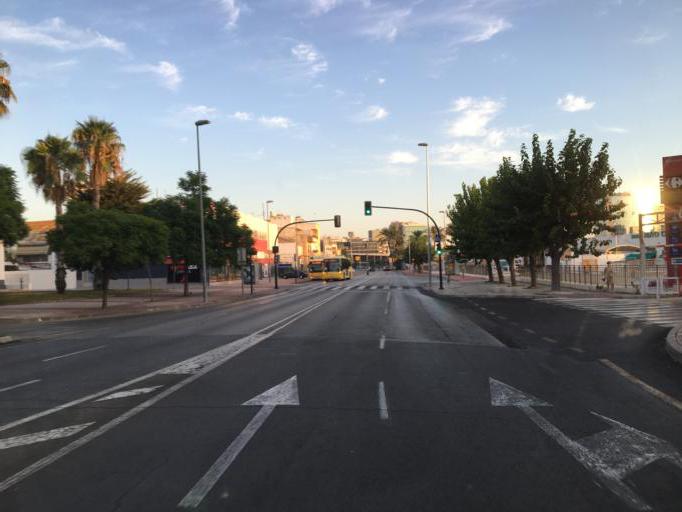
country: ES
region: Murcia
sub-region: Murcia
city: Murcia
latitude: 37.9997
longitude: -1.1433
